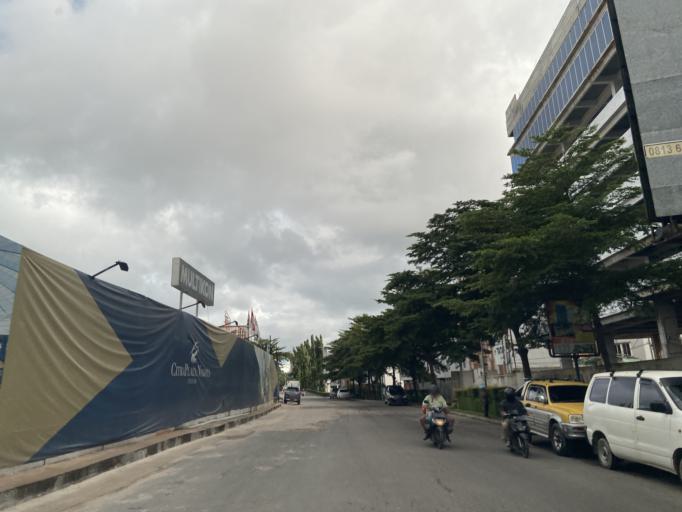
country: SG
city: Singapore
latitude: 1.1438
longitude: 104.0097
